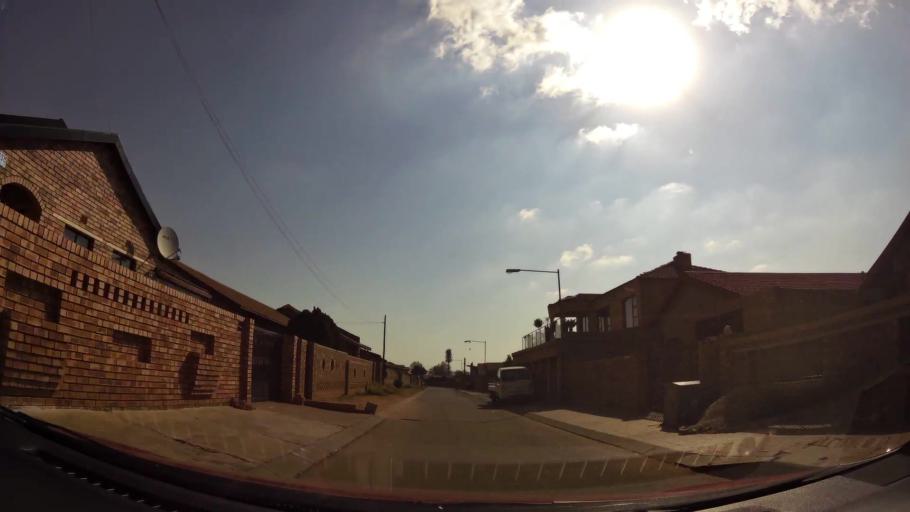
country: ZA
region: Gauteng
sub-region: City of Johannesburg Metropolitan Municipality
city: Johannesburg
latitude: -26.2364
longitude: 27.9541
